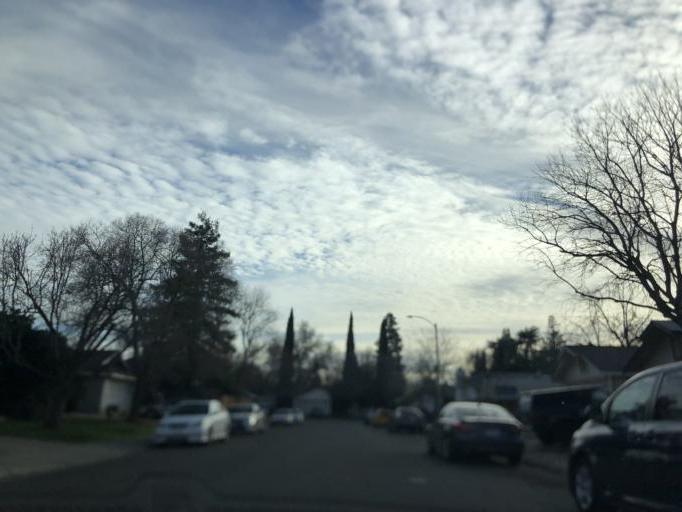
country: US
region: California
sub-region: Yolo County
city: Woodland
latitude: 38.6728
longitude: -121.7550
